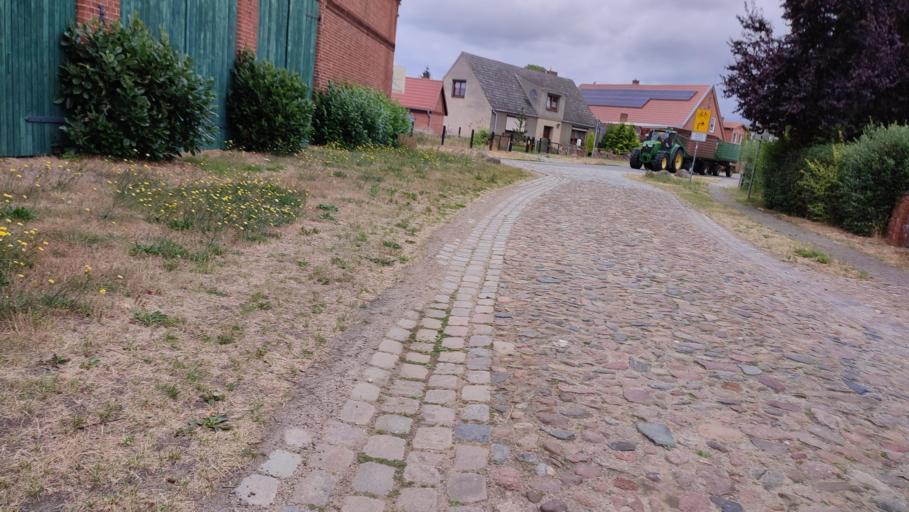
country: DE
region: Lower Saxony
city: Hitzacker
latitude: 53.1818
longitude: 11.1030
